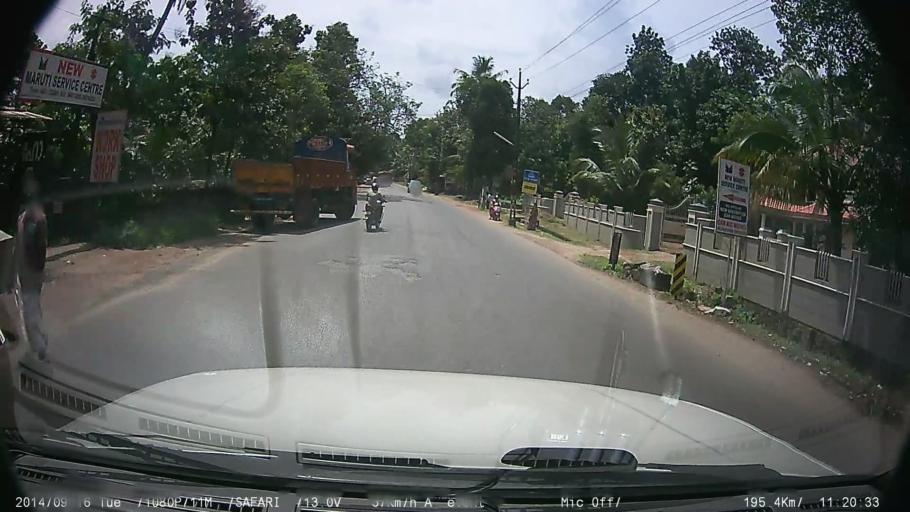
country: IN
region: Kerala
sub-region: Kottayam
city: Changanacheri
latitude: 9.4831
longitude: 76.5257
